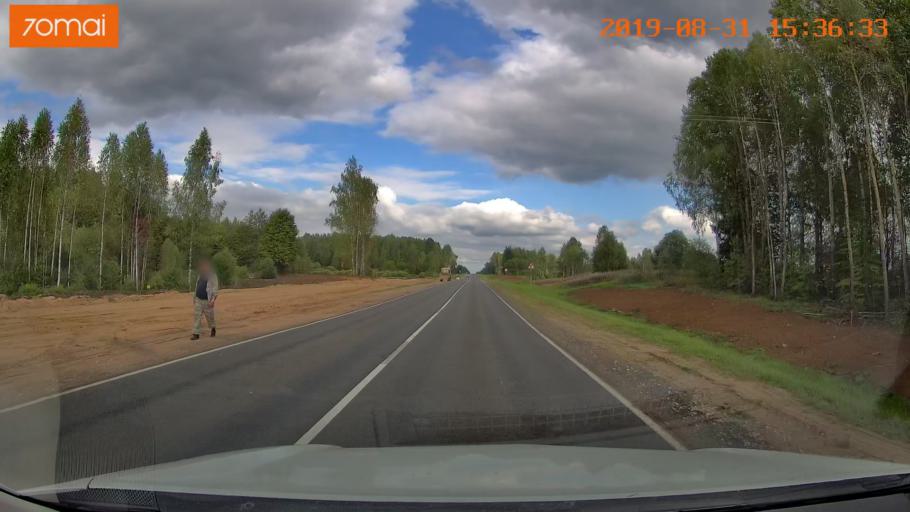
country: RU
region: Kaluga
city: Mosal'sk
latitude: 54.6120
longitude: 34.7617
